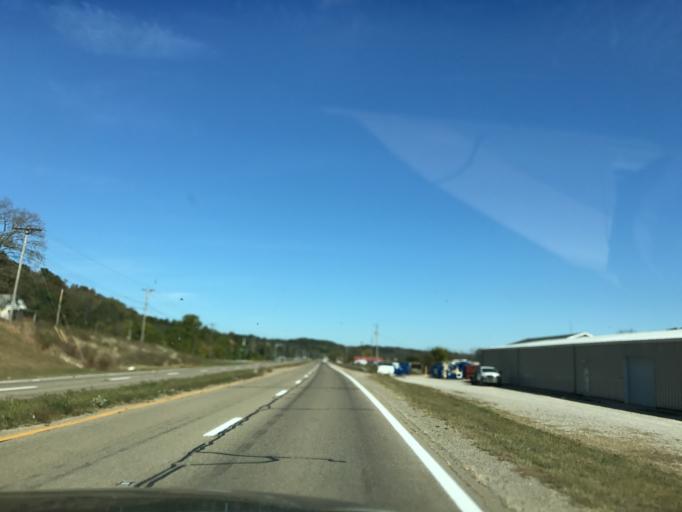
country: US
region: Ohio
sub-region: Muskingum County
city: New Concord
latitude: 40.0033
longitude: -81.6718
